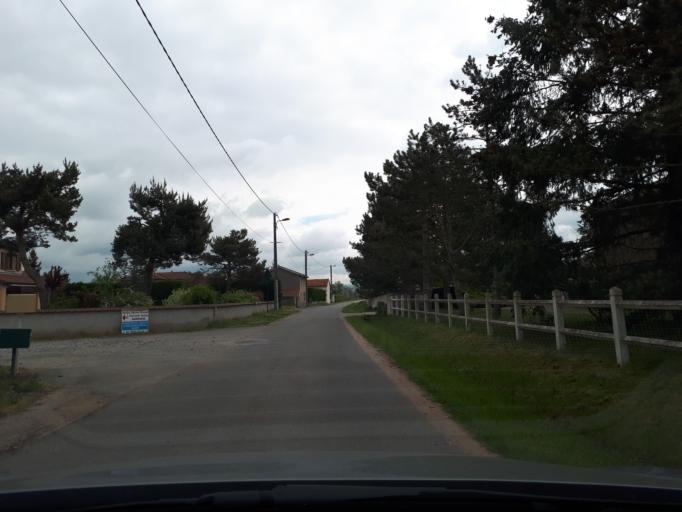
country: FR
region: Rhone-Alpes
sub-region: Departement de la Loire
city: Montrond-les-Bains
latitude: 45.6680
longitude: 4.2099
